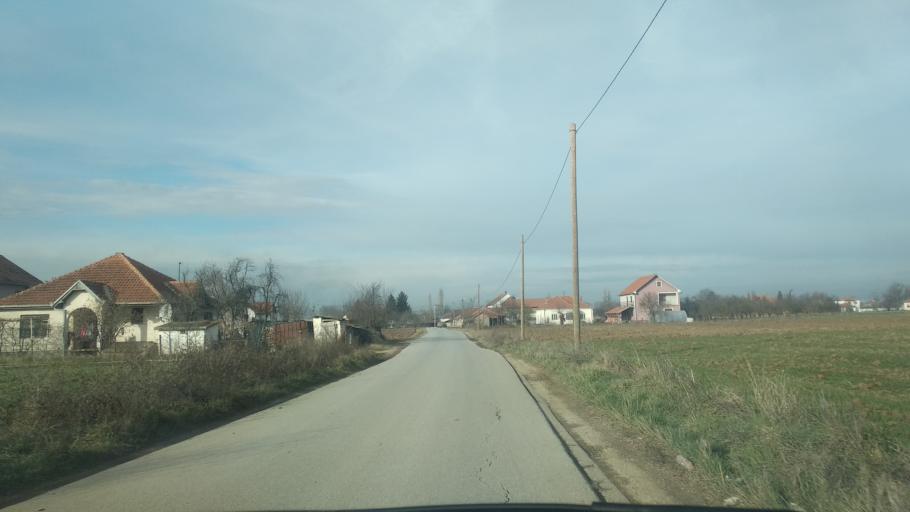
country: XK
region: Pristina
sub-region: Komuna e Gracanices
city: Glanica
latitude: 42.5932
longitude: 21.1182
